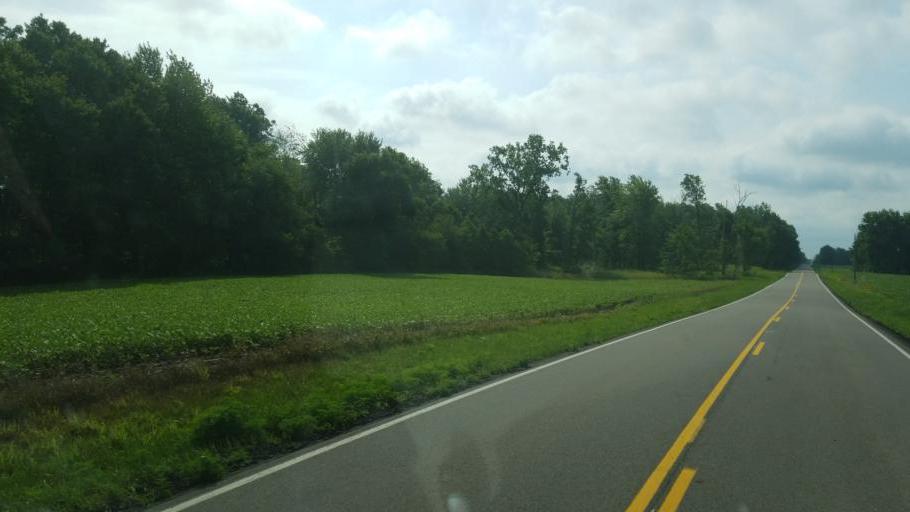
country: US
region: Ohio
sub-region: Knox County
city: Centerburg
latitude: 40.2633
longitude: -82.6024
